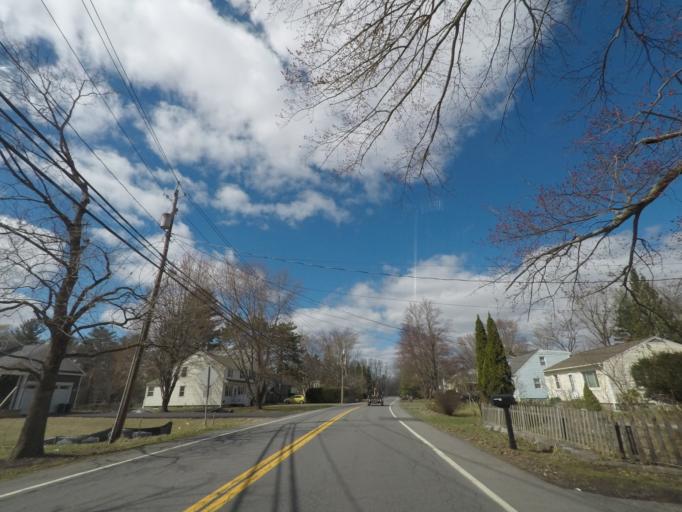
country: US
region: New York
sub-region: Albany County
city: Delmar
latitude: 42.5933
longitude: -73.8339
